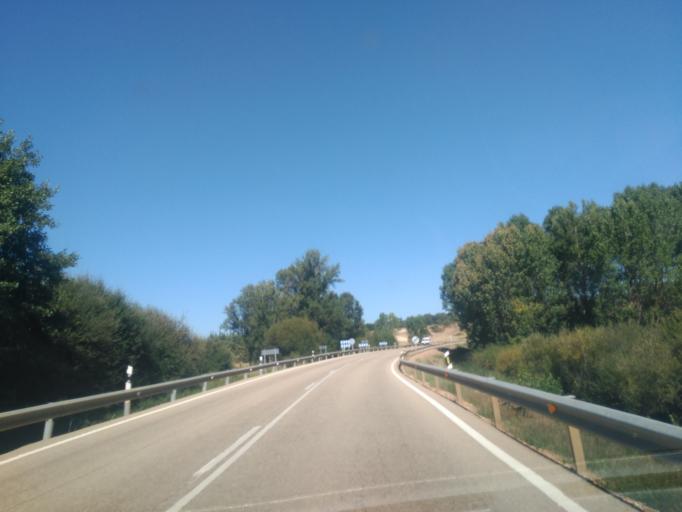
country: ES
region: Castille and Leon
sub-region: Provincia de Zamora
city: Tabara
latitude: 41.8351
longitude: -5.9715
